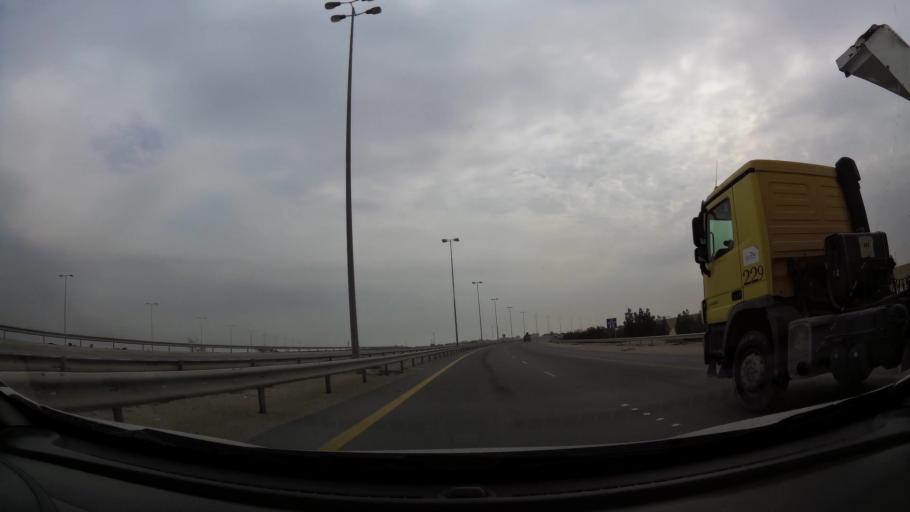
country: BH
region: Northern
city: Sitrah
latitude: 26.0709
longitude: 50.6151
